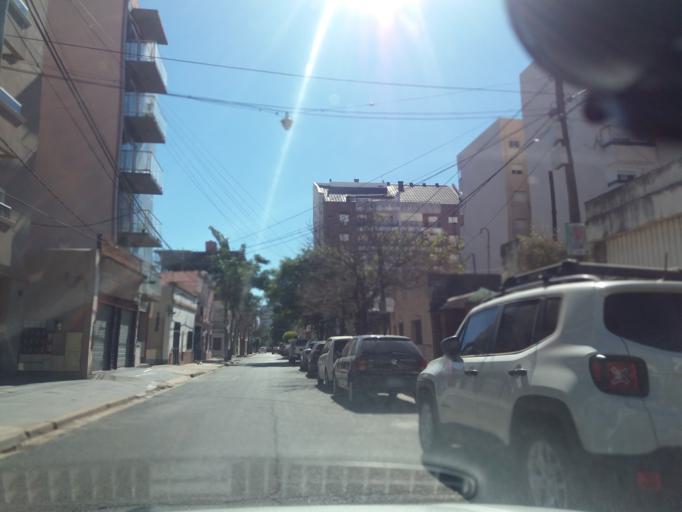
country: AR
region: Corrientes
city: Corrientes
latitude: -27.4687
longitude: -58.8431
